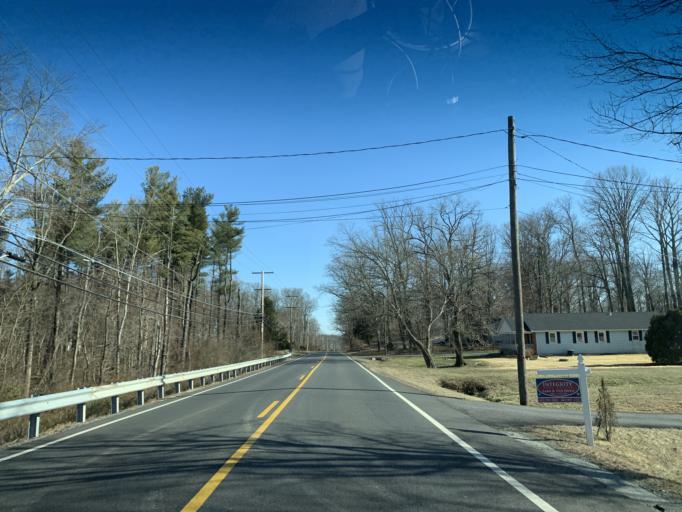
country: US
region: Maryland
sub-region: Cecil County
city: North East
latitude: 39.6609
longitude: -75.8910
